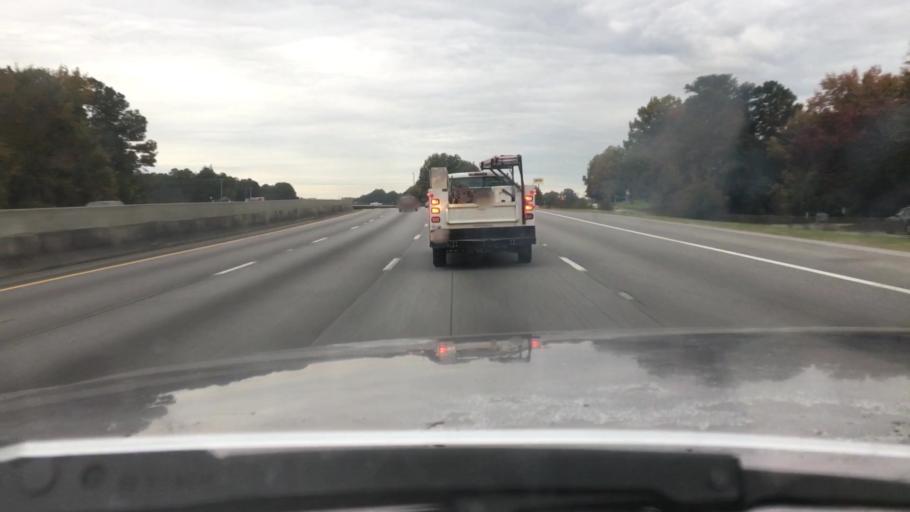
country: US
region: South Carolina
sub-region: Lexington County
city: Saint Andrews
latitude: 34.0342
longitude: -81.1183
